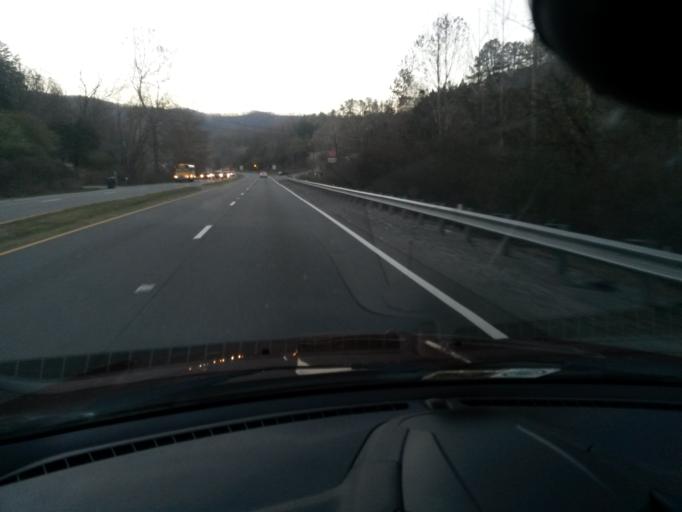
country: US
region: Virginia
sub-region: Roanoke County
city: Narrows
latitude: 37.1888
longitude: -79.9363
